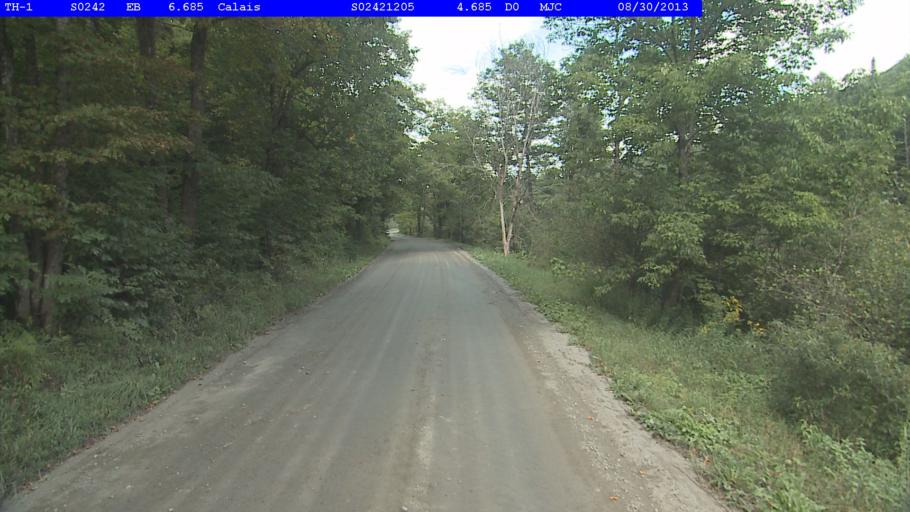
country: US
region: Vermont
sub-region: Caledonia County
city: Hardwick
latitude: 44.3735
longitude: -72.4602
